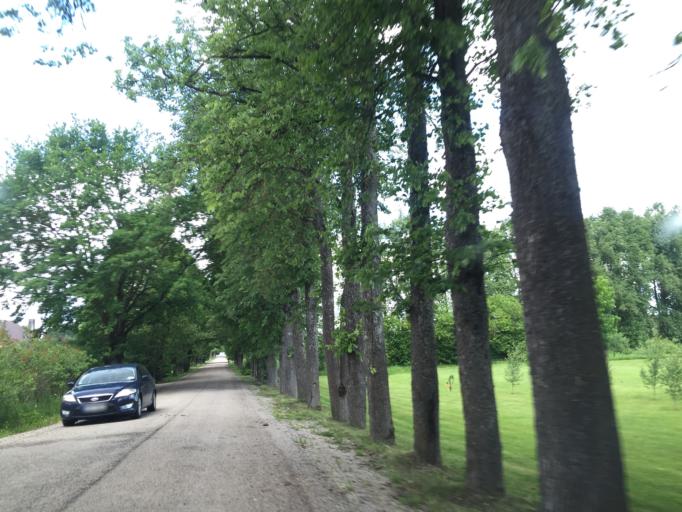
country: LV
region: Lecava
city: Iecava
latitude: 56.6811
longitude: 24.2454
